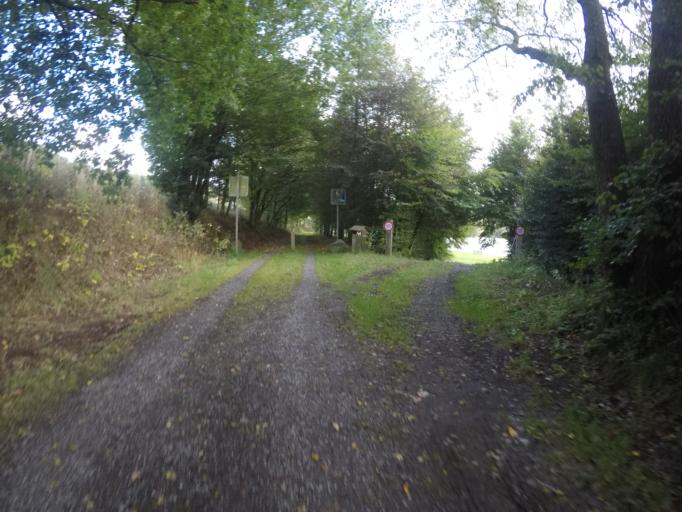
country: BE
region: Wallonia
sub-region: Province du Luxembourg
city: Bastogne
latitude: 49.9325
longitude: 5.6974
